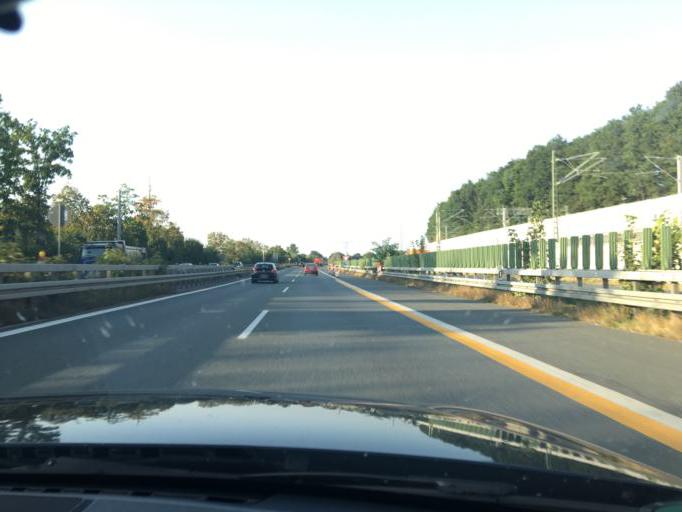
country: DE
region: Bavaria
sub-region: Regierungsbezirk Mittelfranken
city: Mohrendorf
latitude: 49.6164
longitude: 11.0015
